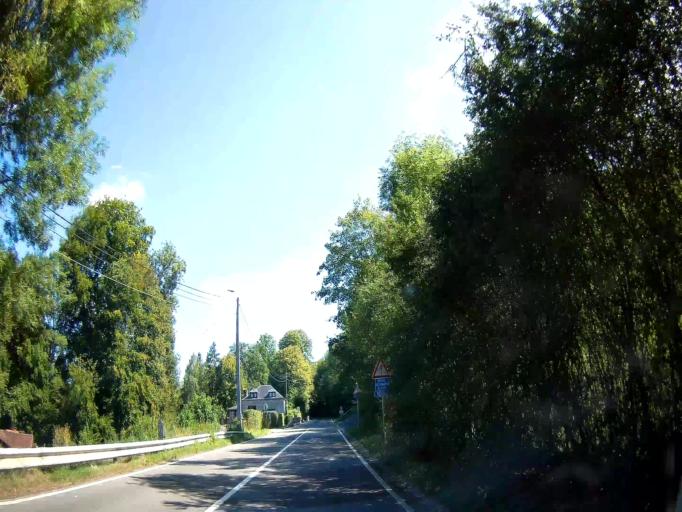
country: BE
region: Wallonia
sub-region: Province de Namur
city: Hastiere-Lavaux
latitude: 50.2132
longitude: 4.8369
